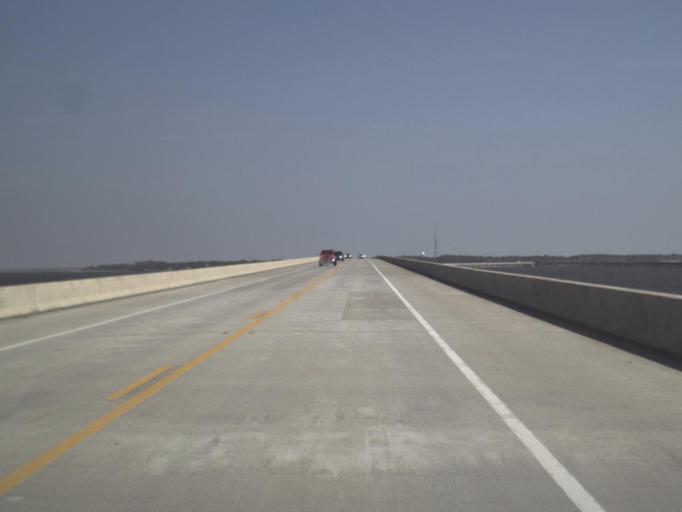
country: US
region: Florida
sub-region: Franklin County
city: Eastpoint
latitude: 29.7048
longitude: -84.8905
